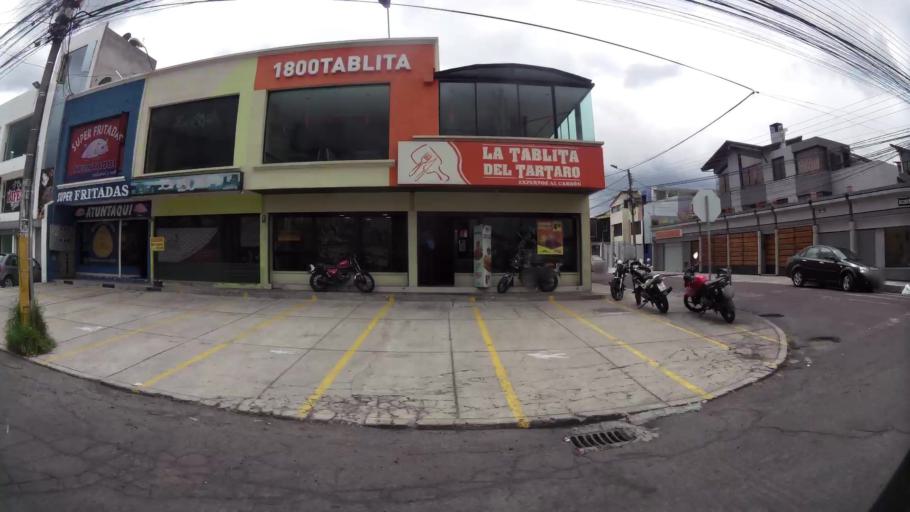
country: EC
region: Pichincha
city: Quito
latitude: -0.1674
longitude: -78.4821
